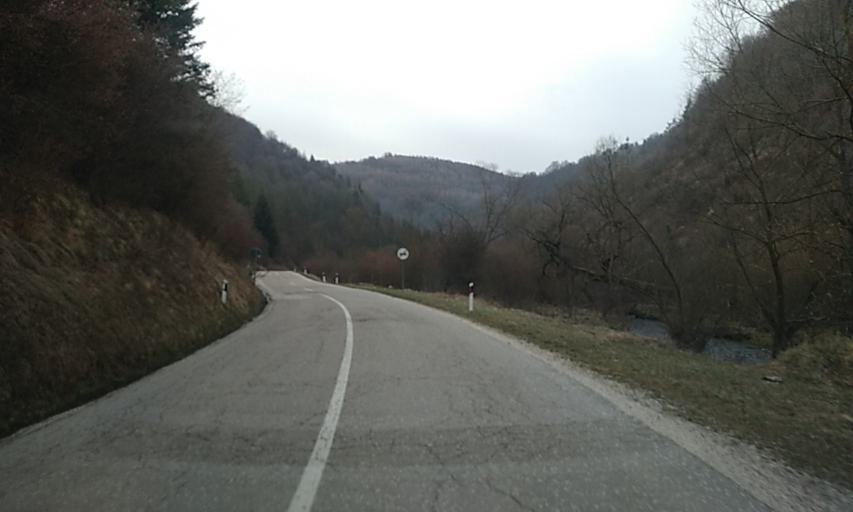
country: RS
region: Central Serbia
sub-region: Pcinjski Okrug
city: Bosilegrad
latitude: 42.6070
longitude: 22.4007
